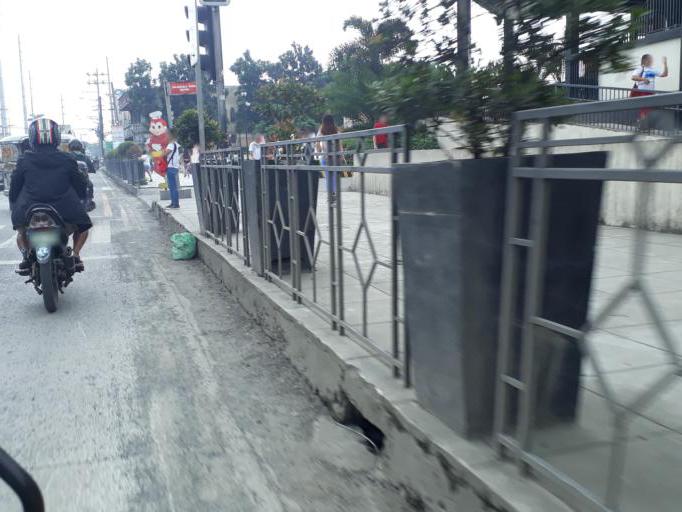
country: PH
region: Calabarzon
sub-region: Province of Rizal
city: Valenzuela
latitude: 14.6925
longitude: 120.9697
